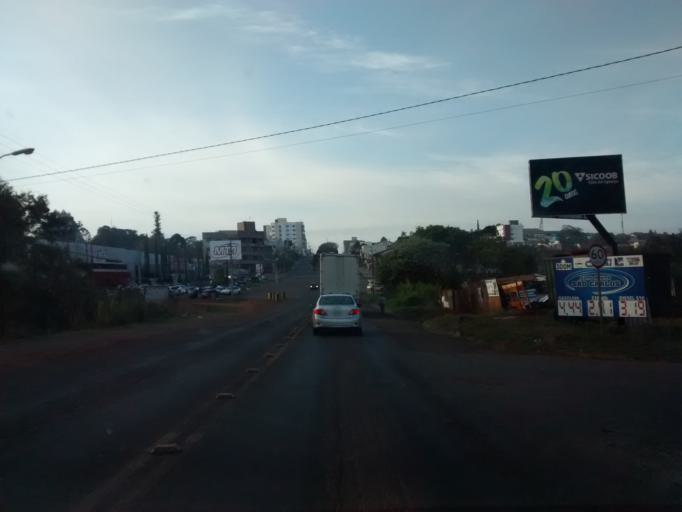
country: BR
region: Parana
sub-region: Francisco Beltrao
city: Francisco Beltrao
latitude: -26.1428
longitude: -53.0289
